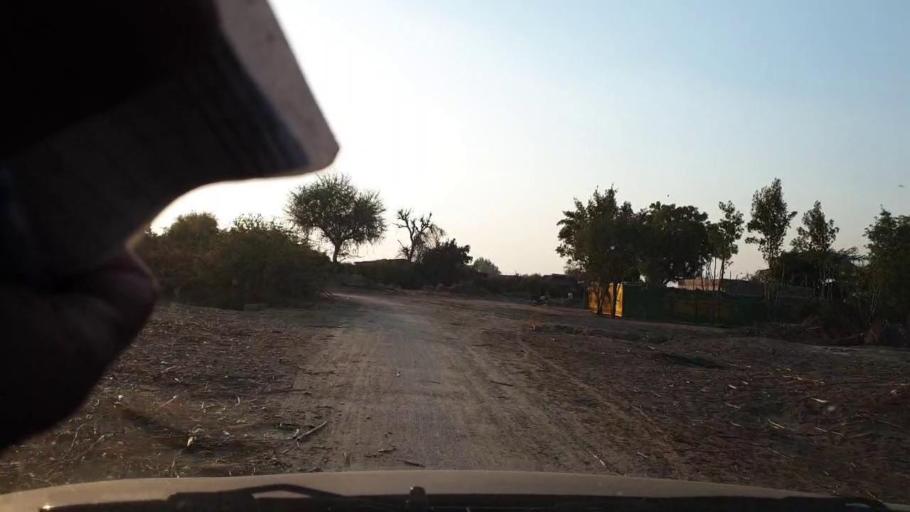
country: PK
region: Sindh
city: Jhol
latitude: 25.9112
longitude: 68.9303
